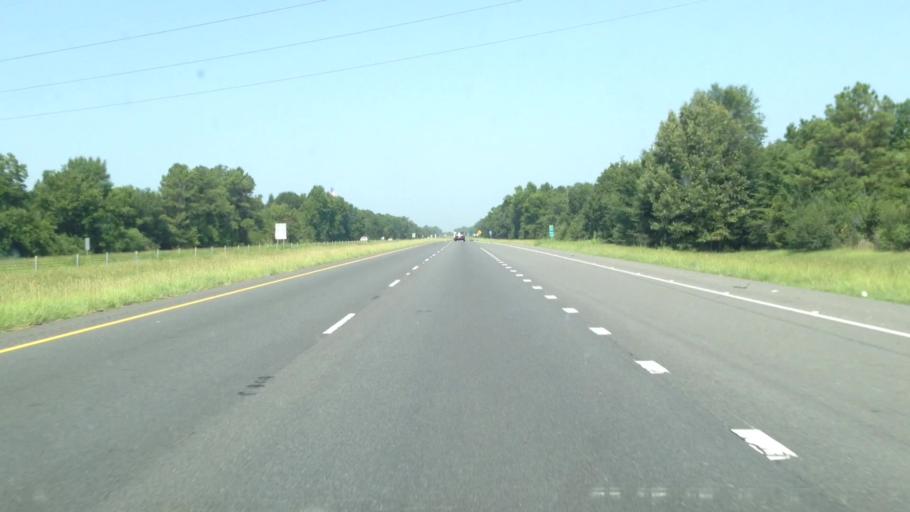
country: US
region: Louisiana
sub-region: Richland Parish
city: Delhi
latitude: 32.4522
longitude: -91.5860
